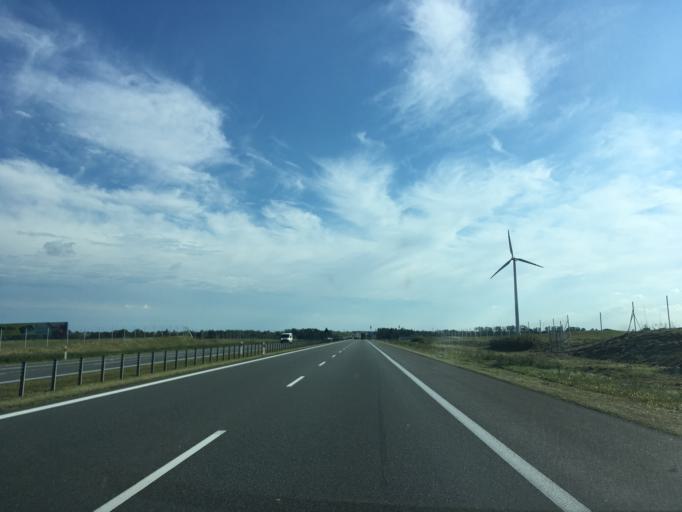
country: PL
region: Kujawsko-Pomorskie
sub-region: Powiat chelminski
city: Lisewo
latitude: 53.3684
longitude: 18.6951
